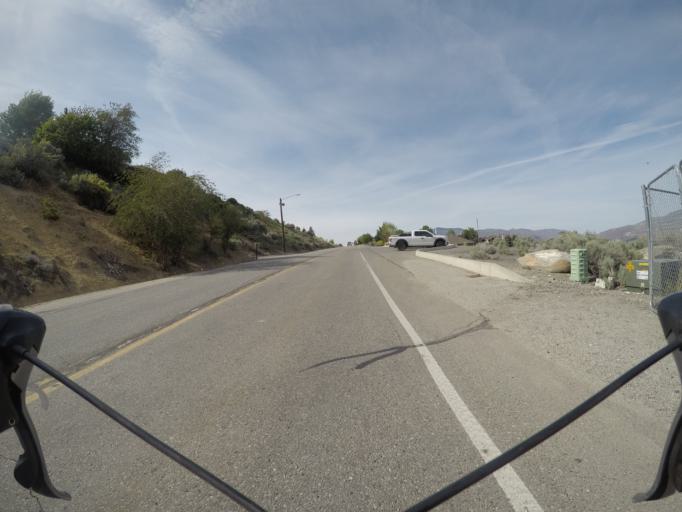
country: US
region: Washington
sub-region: Chelan County
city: Wenatchee
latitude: 47.4100
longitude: -120.3416
